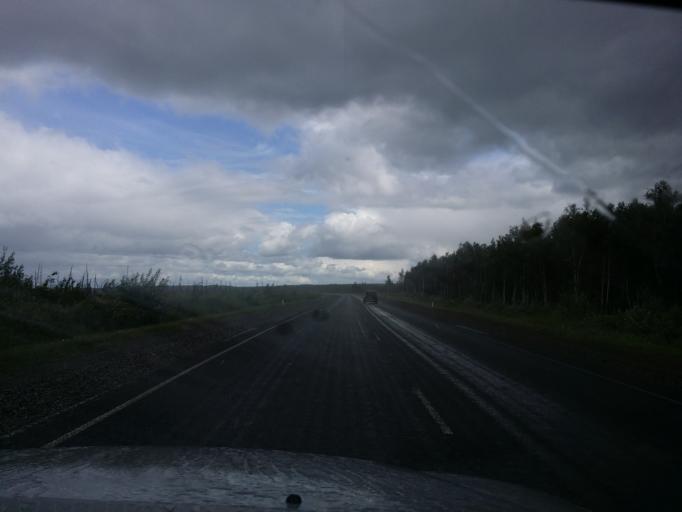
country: RU
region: Tjumen
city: Tobol'sk
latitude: 58.4337
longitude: 68.4392
